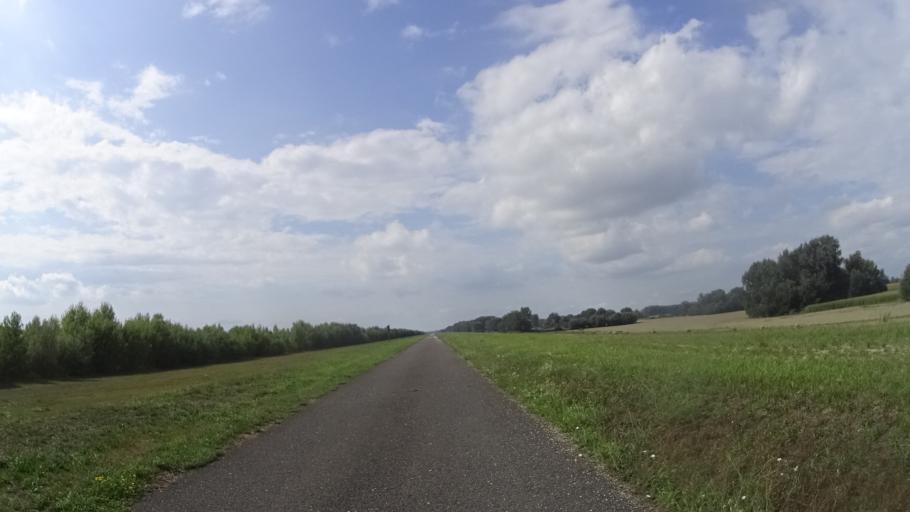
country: SK
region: Trnavsky
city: Gabcikovo
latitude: 47.8368
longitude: 17.5936
